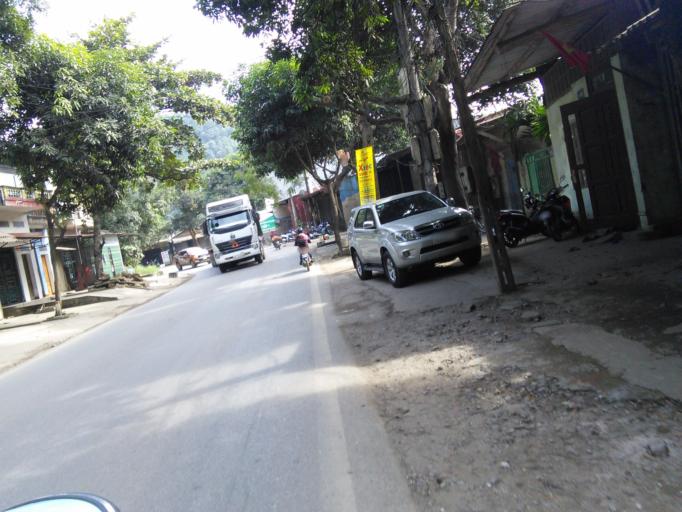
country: VN
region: Lao Cai
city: Lao Cai
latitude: 22.4731
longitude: 103.9696
